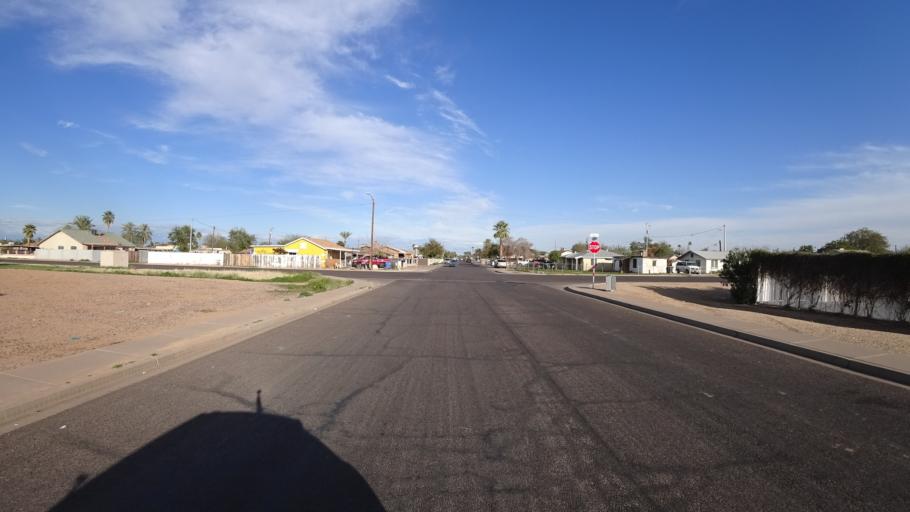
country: US
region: Arizona
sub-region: Maricopa County
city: Phoenix
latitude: 33.4551
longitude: -112.1395
